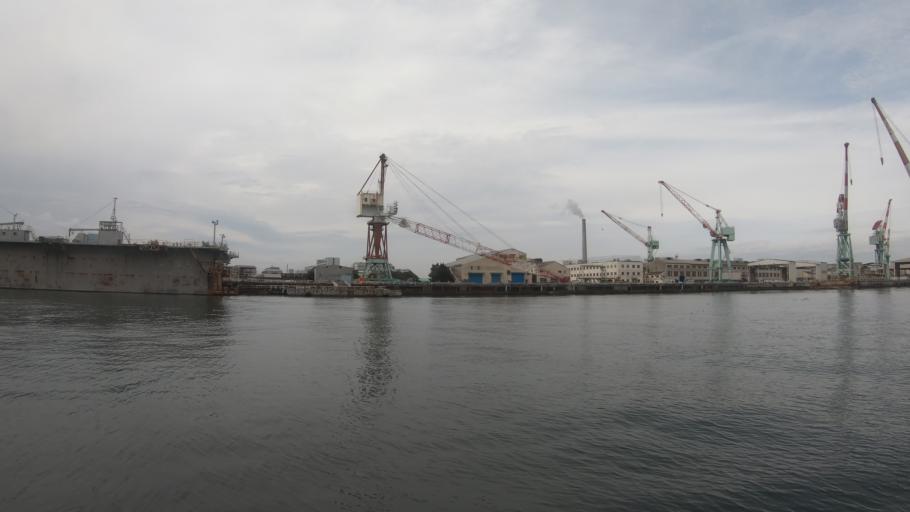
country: JP
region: Kanagawa
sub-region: Kawasaki-shi
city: Kawasaki
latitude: 35.4897
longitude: 139.6921
